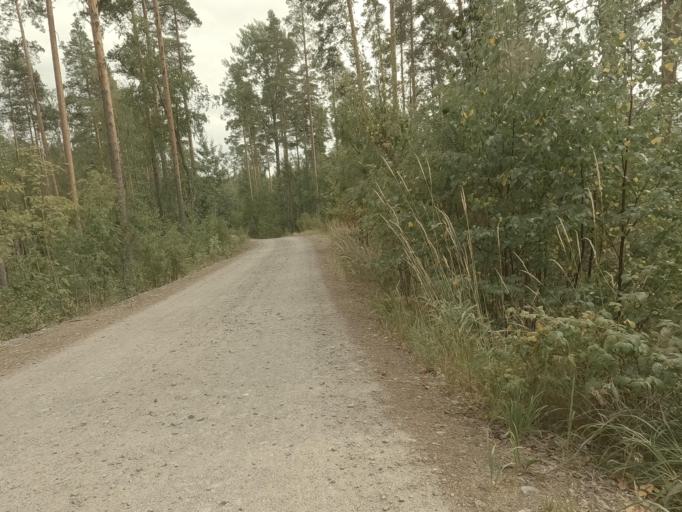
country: RU
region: Leningrad
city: Kamennogorsk
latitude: 60.9762
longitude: 29.1733
